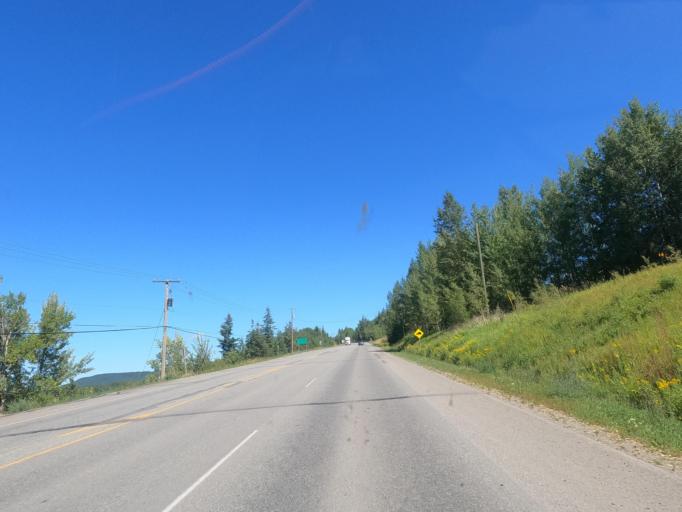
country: CA
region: British Columbia
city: Quesnel
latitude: 53.0171
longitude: -122.4949
